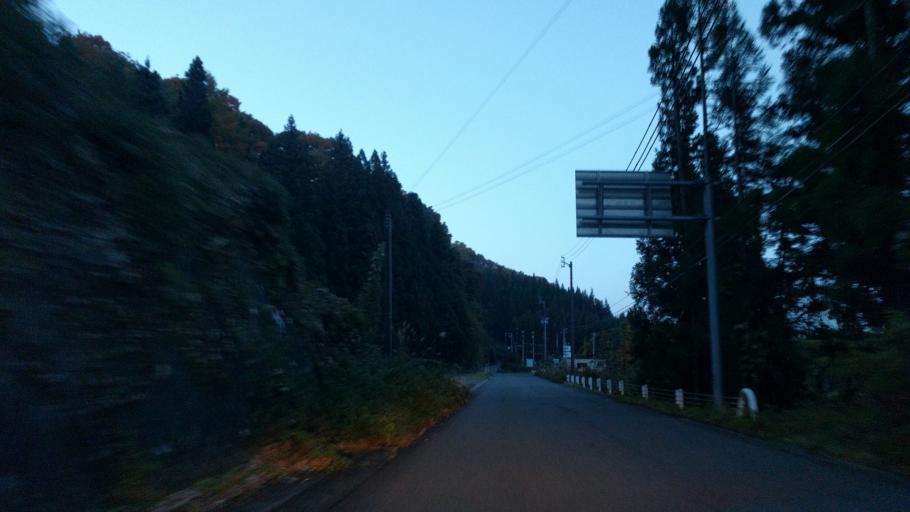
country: JP
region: Fukushima
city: Kitakata
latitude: 37.5351
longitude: 139.7188
